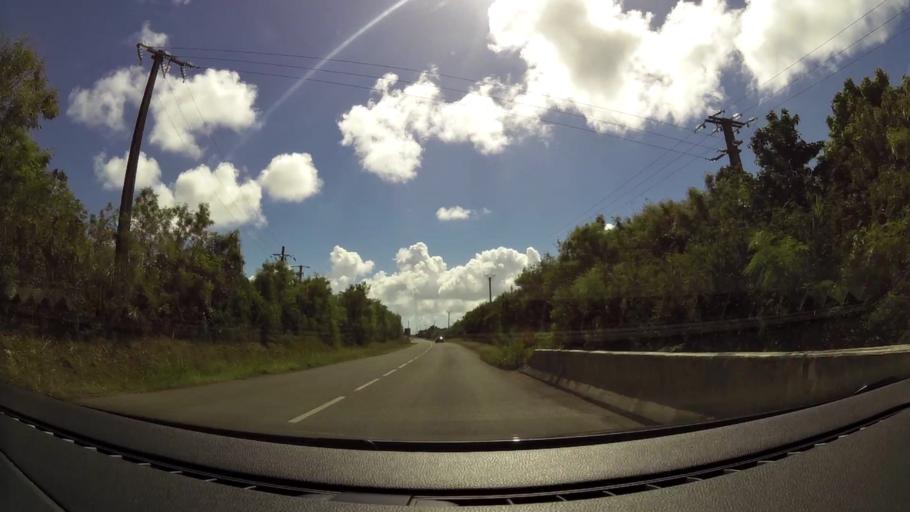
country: GP
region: Guadeloupe
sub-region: Guadeloupe
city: Petit-Canal
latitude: 16.4274
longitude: -61.4762
